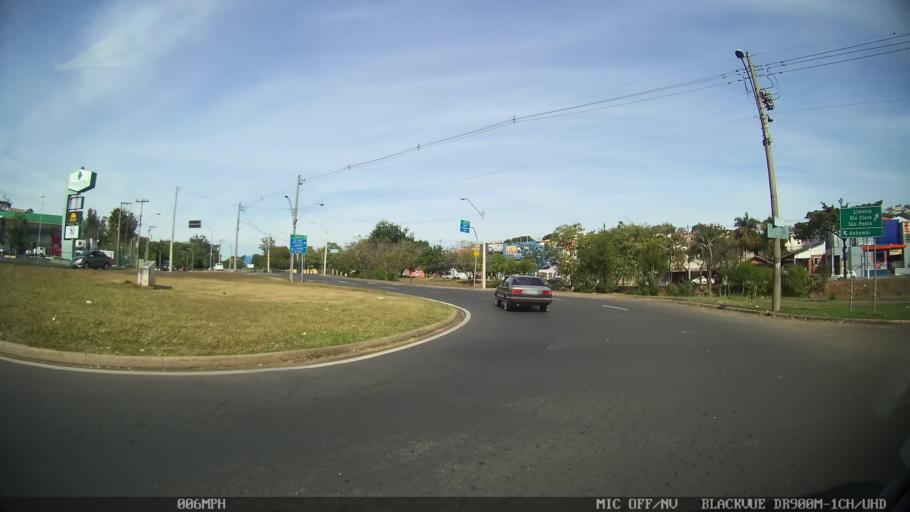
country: BR
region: Sao Paulo
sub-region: Piracicaba
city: Piracicaba
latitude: -22.7405
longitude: -47.6686
